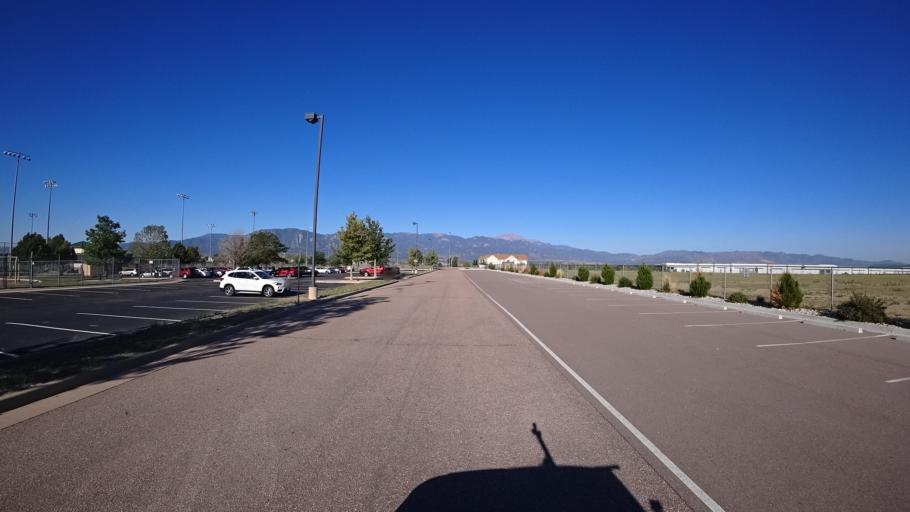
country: US
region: Colorado
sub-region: El Paso County
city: Security-Widefield
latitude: 38.7883
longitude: -104.7234
